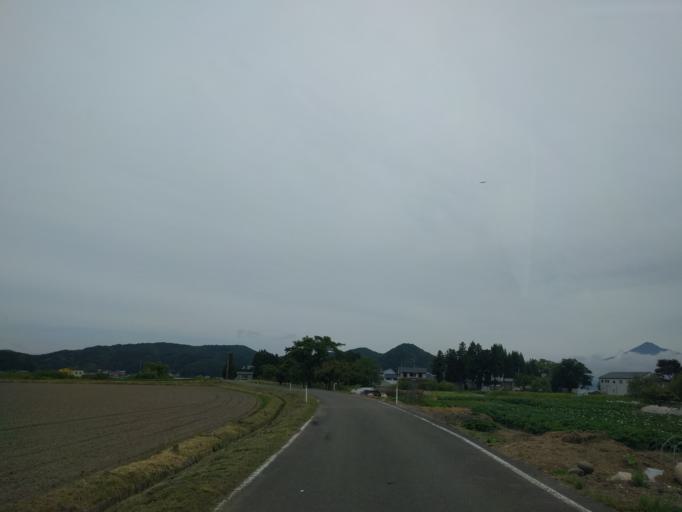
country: JP
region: Fukushima
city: Inawashiro
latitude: 37.4559
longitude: 140.0488
